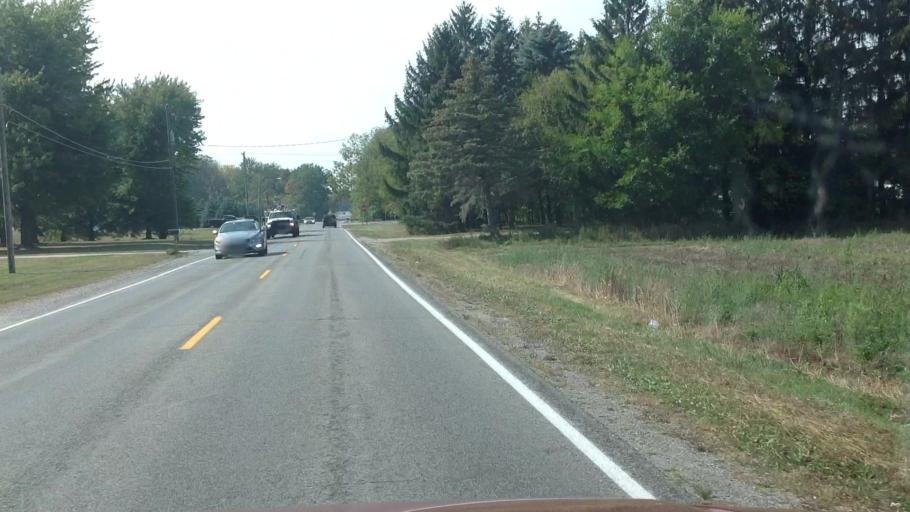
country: US
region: Michigan
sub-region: Saginaw County
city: Shields
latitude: 43.4657
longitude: -84.0318
